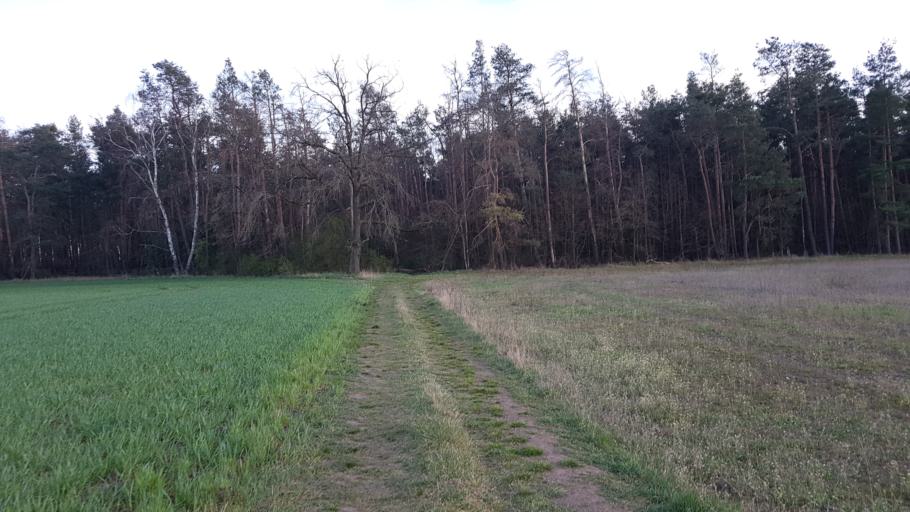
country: DE
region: Brandenburg
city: Schilda
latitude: 51.6028
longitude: 13.3921
